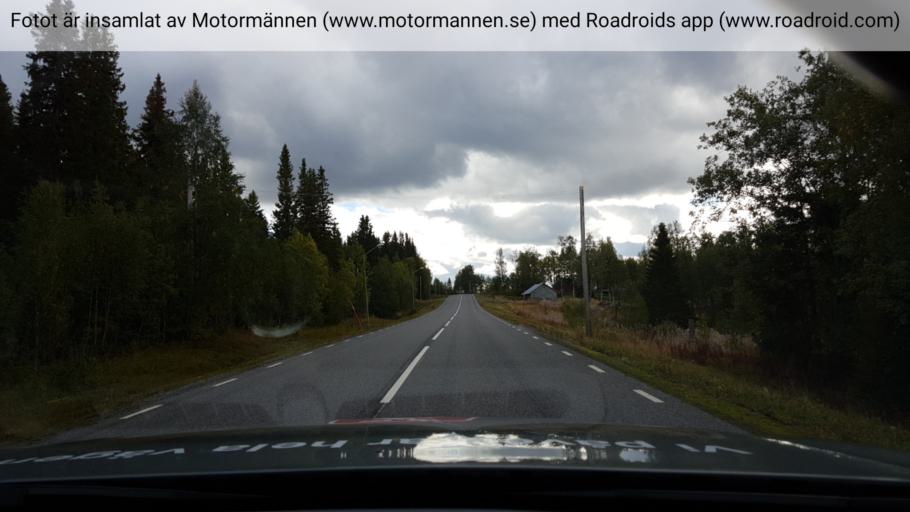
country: SE
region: Jaemtland
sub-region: Are Kommun
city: Are
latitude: 63.6499
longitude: 13.0681
